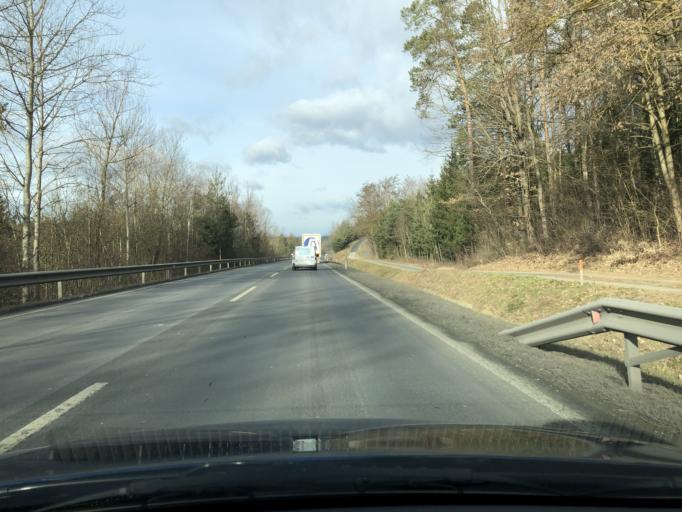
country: AT
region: Burgenland
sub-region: Politischer Bezirk Oberwart
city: Oberwart
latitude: 47.2756
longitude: 16.1986
